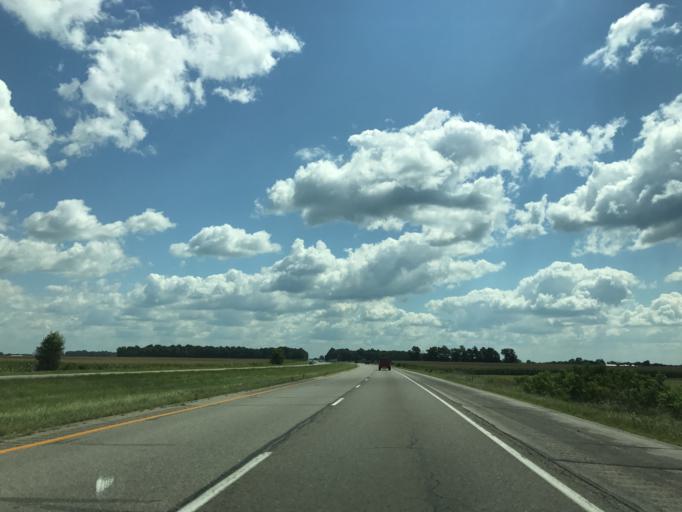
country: US
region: Indiana
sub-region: Marshall County
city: Plymouth
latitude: 41.3346
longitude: -86.2491
